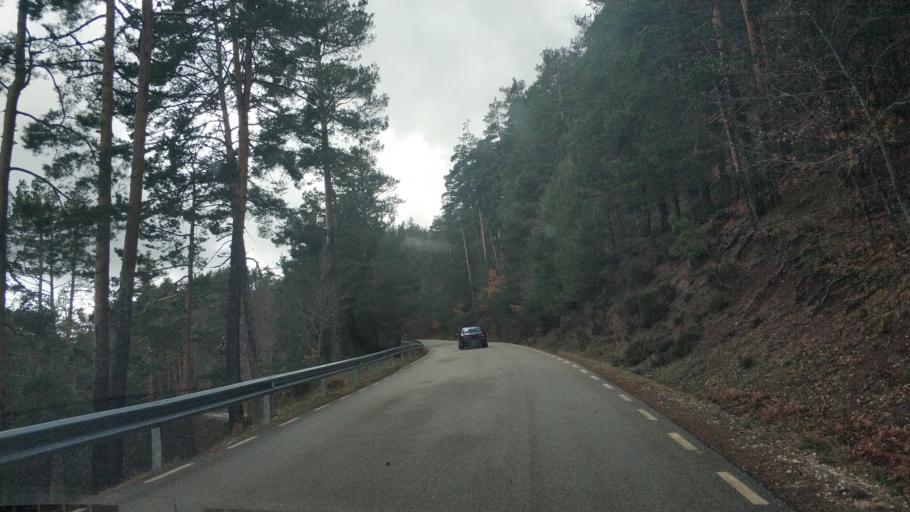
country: ES
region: Castille and Leon
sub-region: Provincia de Burgos
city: Neila
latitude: 42.0459
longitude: -3.0105
